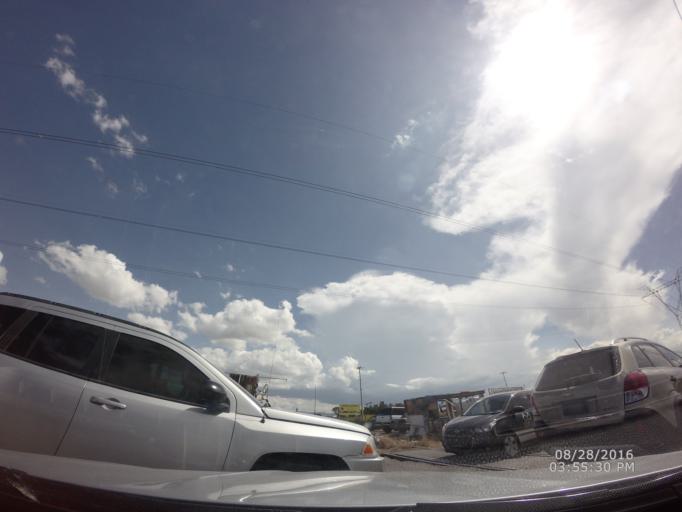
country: MX
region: Hidalgo
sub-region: Mineral de la Reforma
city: Los Tuzos
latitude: 20.0364
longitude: -98.7483
